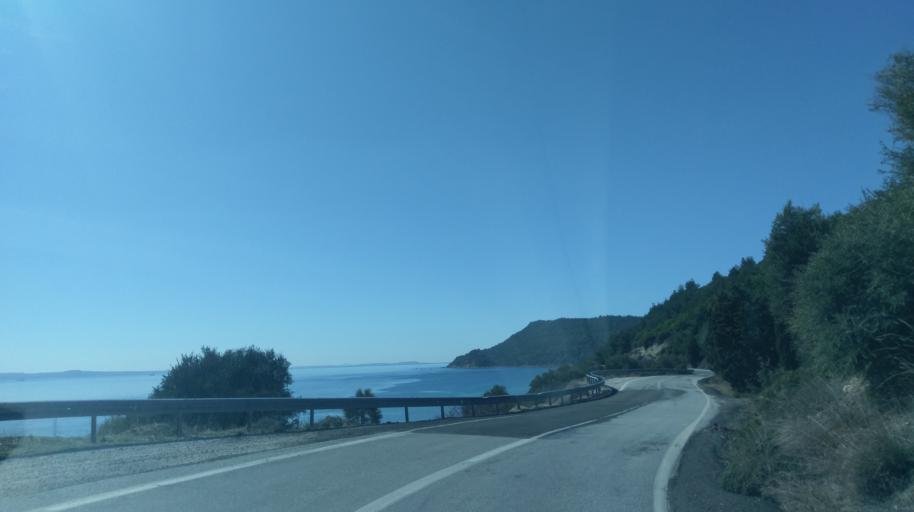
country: TR
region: Canakkale
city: Eceabat
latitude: 40.1064
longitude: 26.3277
